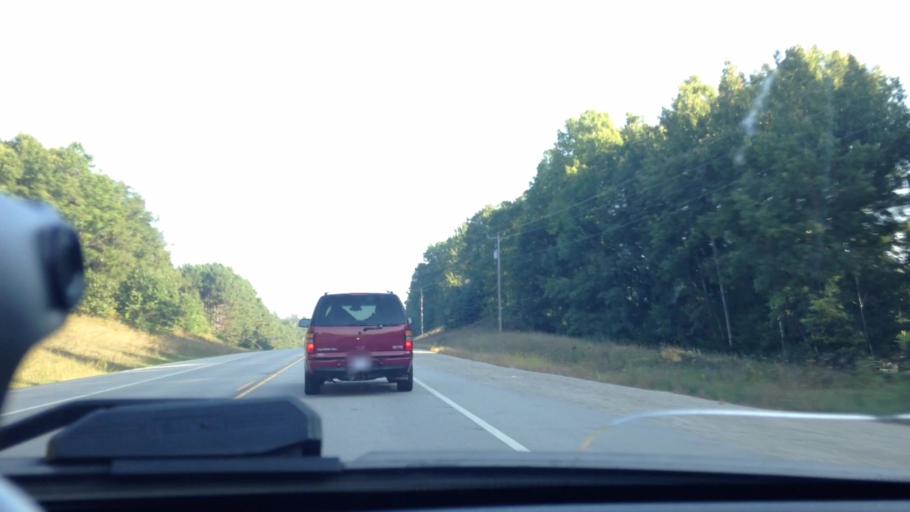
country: US
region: Wisconsin
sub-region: Marinette County
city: Peshtigo
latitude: 45.1654
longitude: -87.9964
